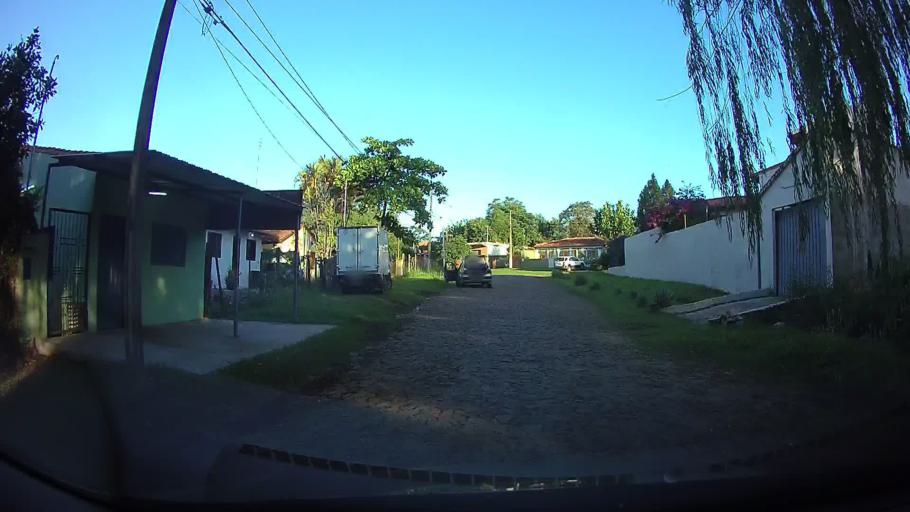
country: PY
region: Central
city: San Lorenzo
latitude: -25.2626
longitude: -57.4841
